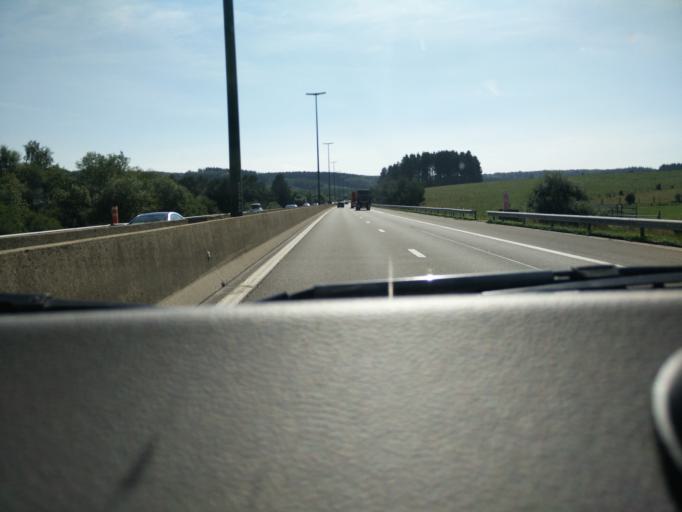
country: BE
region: Wallonia
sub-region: Province du Luxembourg
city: Leglise
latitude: 49.7725
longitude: 5.5497
